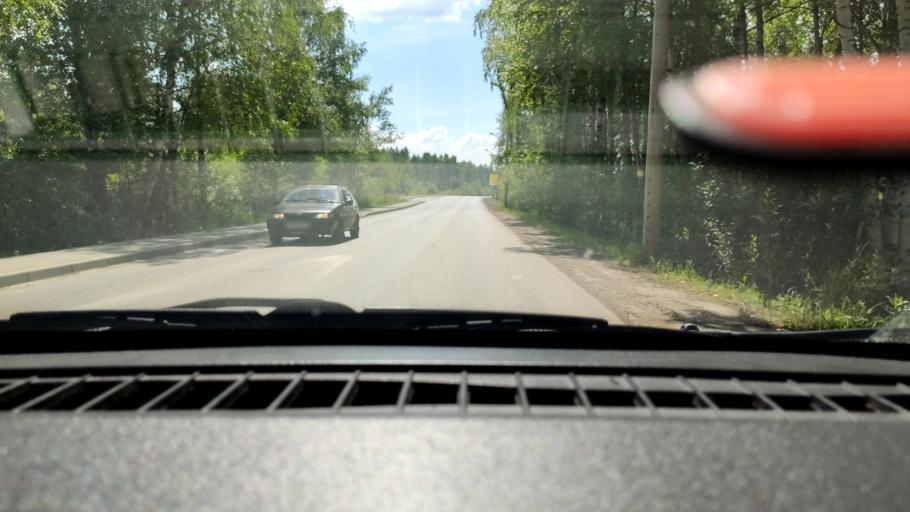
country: RU
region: Perm
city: Perm
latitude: 58.1471
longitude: 56.3032
